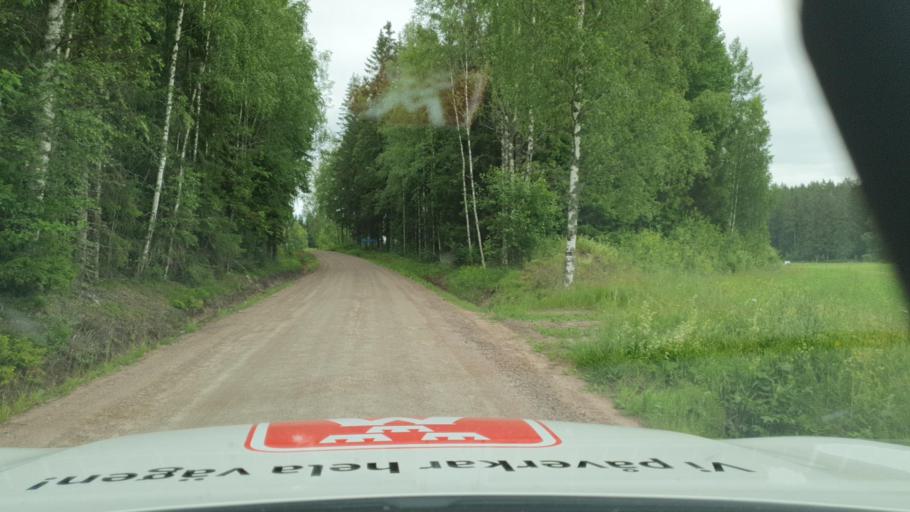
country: SE
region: Vaermland
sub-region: Filipstads Kommun
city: Filipstad
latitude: 59.5499
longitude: 13.9789
